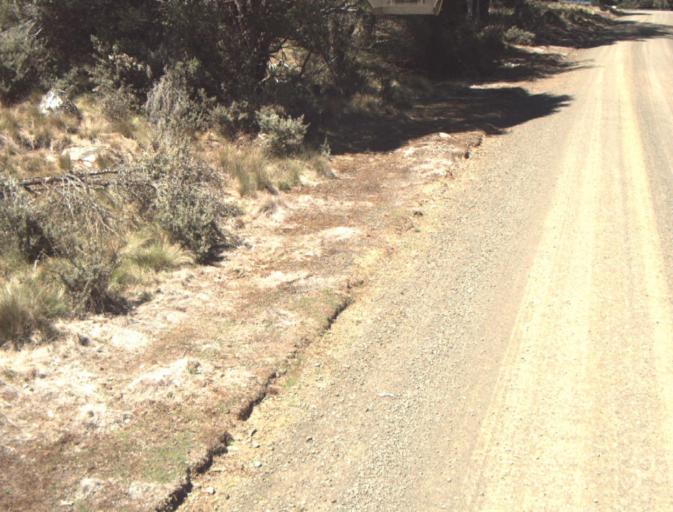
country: AU
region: Tasmania
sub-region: Dorset
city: Scottsdale
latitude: -41.3669
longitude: 147.4303
